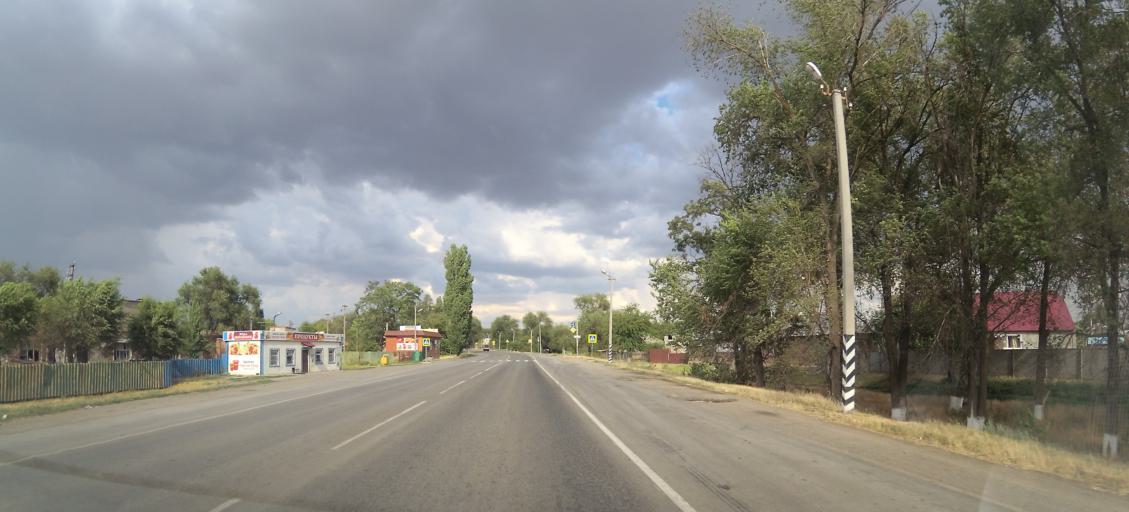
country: RU
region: Rostov
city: Zimovniki
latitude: 47.1462
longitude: 42.4544
